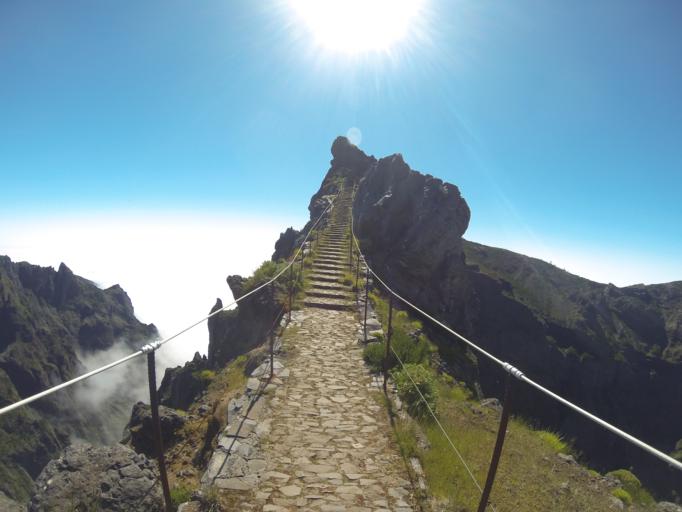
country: PT
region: Madeira
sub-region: Camara de Lobos
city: Curral das Freiras
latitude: 32.7391
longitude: -16.9363
